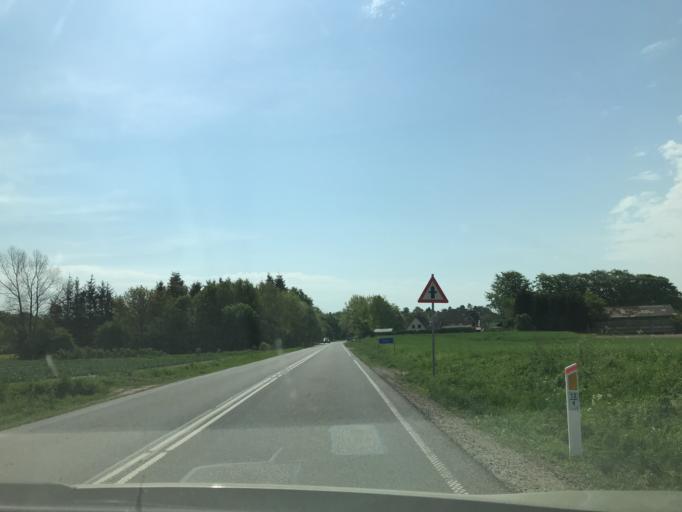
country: DK
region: South Denmark
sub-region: Middelfart Kommune
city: Ejby
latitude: 55.3684
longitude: 9.9248
